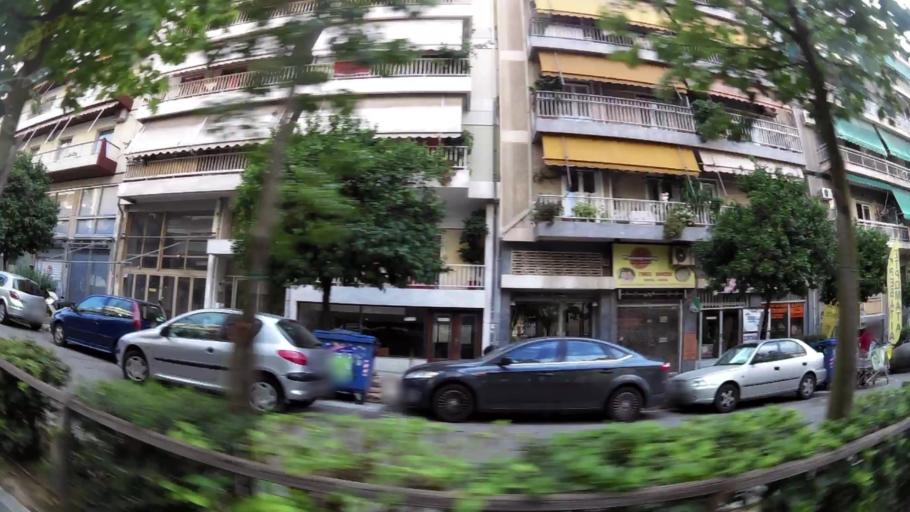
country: GR
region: Attica
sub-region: Nomarchia Athinas
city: Kallithea
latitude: 37.9499
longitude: 23.7036
